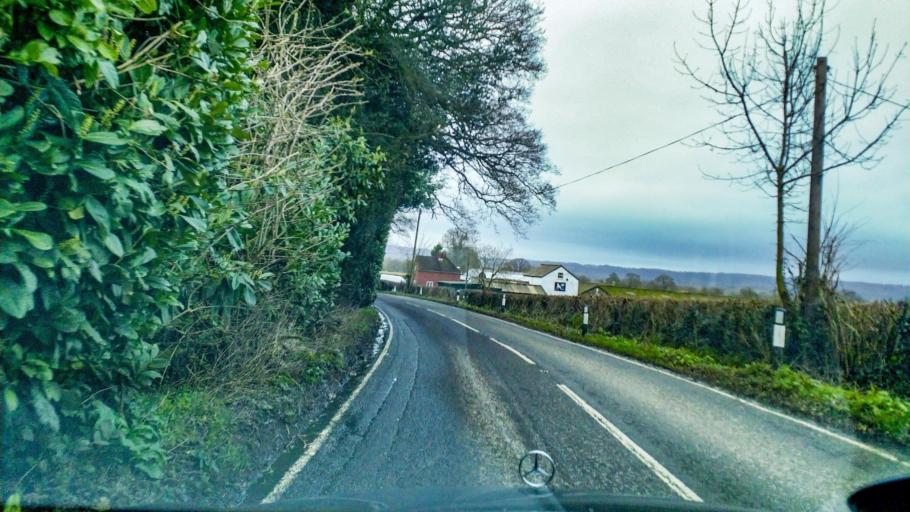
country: GB
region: England
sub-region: Surrey
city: Reigate
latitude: 51.1956
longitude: -0.2420
